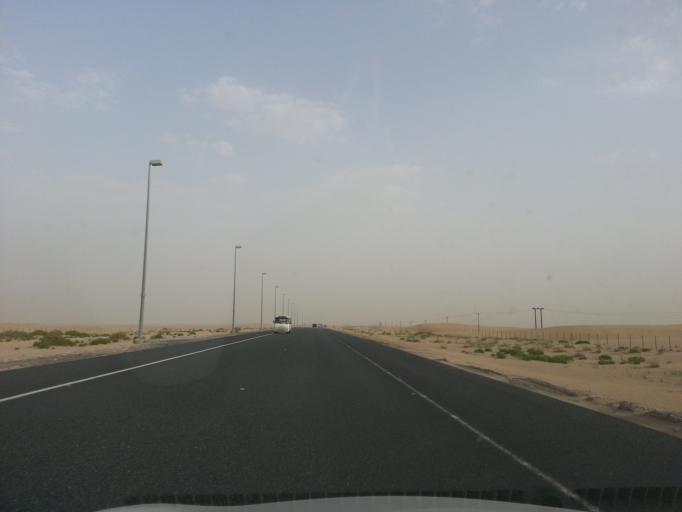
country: AE
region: Dubai
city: Dubai
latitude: 24.7149
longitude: 55.1289
